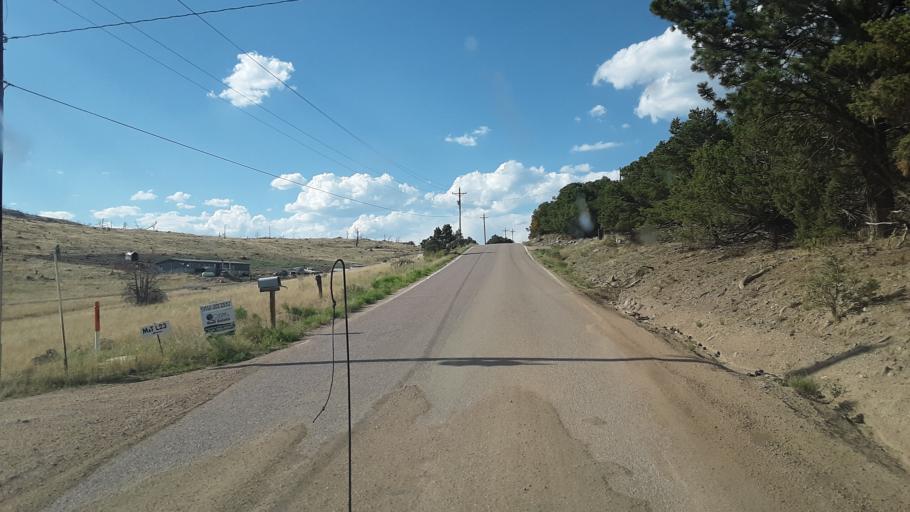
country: US
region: Colorado
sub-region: Custer County
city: Westcliffe
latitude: 38.3211
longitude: -105.4874
